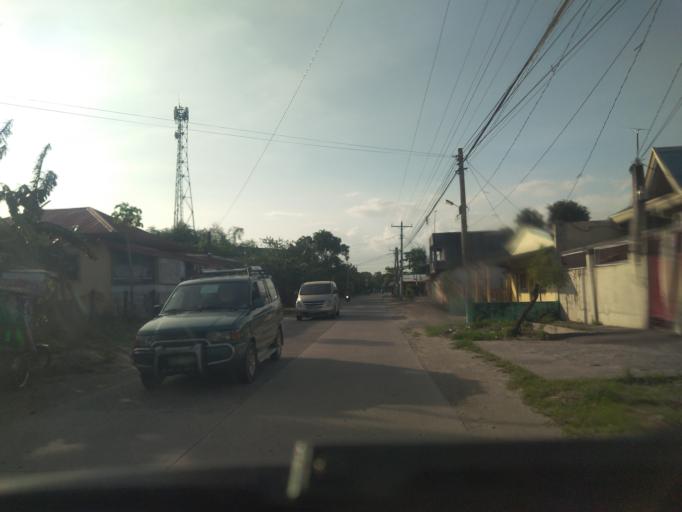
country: PH
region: Central Luzon
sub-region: Province of Pampanga
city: Bulaon
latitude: 15.0890
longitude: 120.6903
